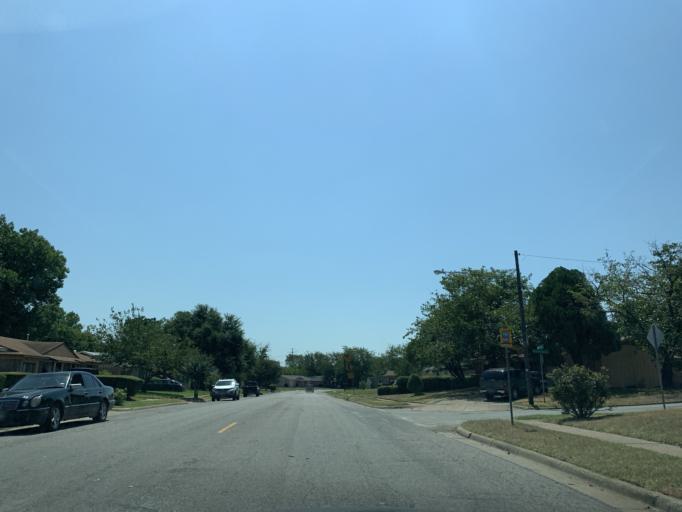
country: US
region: Texas
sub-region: Dallas County
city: Hutchins
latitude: 32.6776
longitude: -96.7495
